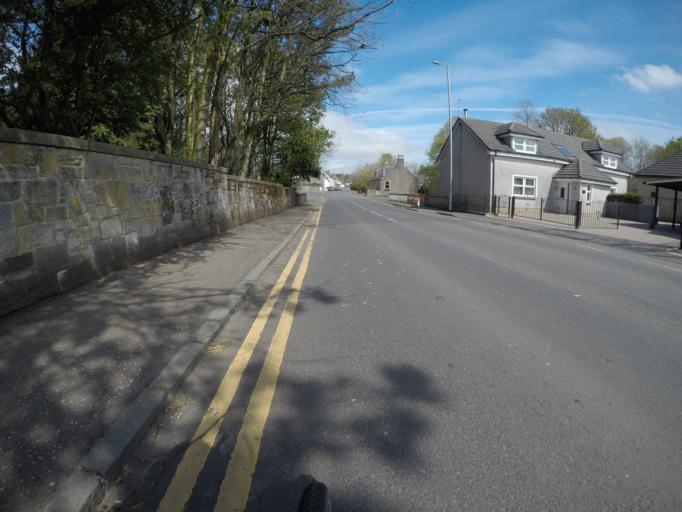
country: GB
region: Scotland
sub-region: East Ayrshire
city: Stewarton
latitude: 55.6831
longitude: -4.5099
